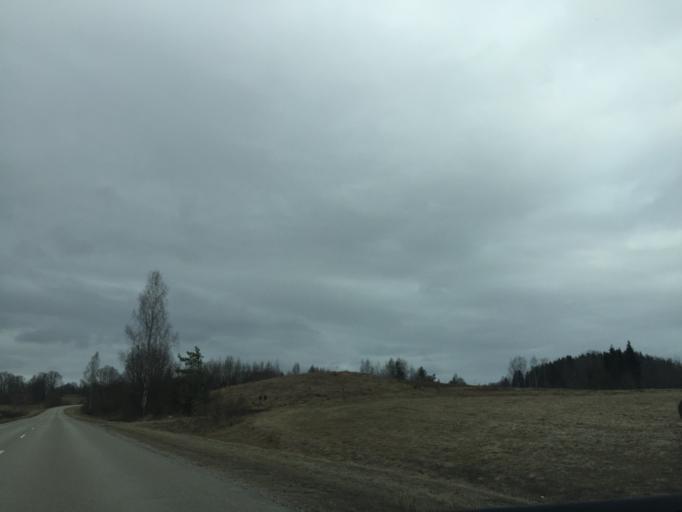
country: LV
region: Kraslavas Rajons
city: Kraslava
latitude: 55.9533
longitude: 27.1626
